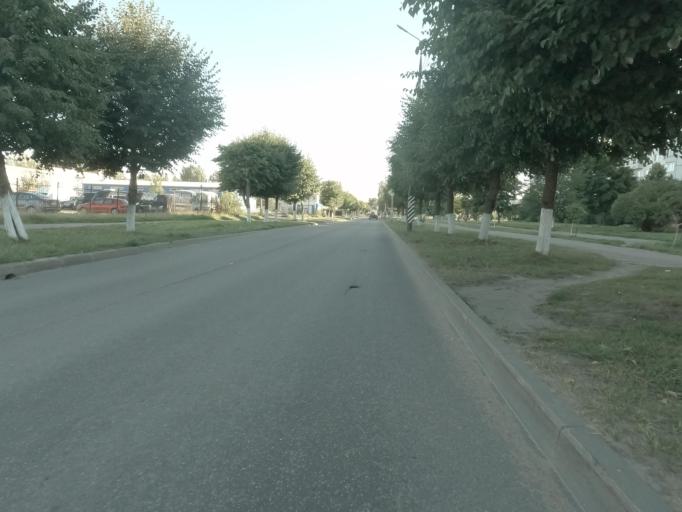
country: RU
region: Leningrad
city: Kirovsk
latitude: 59.8828
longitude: 30.9989
